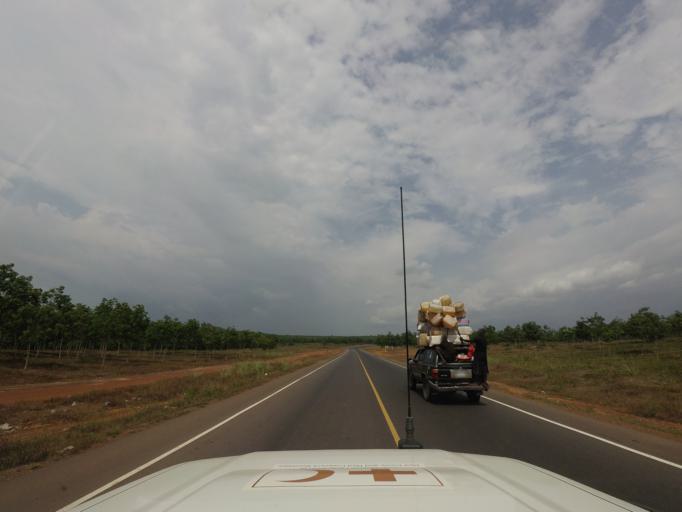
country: LR
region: Margibi
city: Kakata
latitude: 6.4495
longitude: -10.4392
